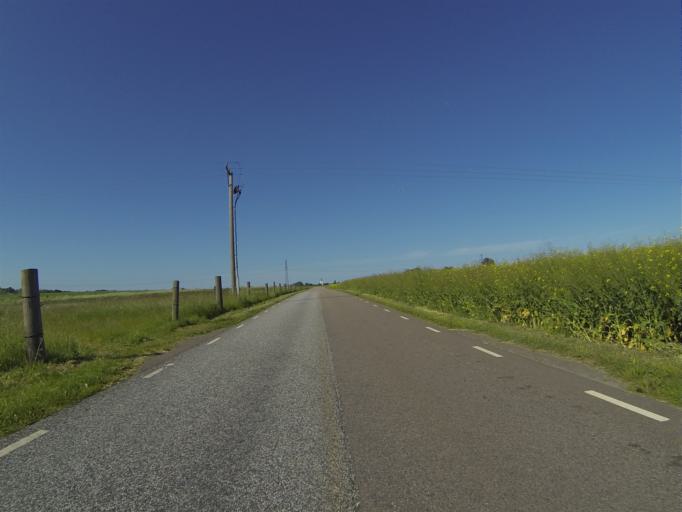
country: SE
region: Skane
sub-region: Staffanstorps Kommun
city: Hjaerup
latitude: 55.6119
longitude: 13.1489
